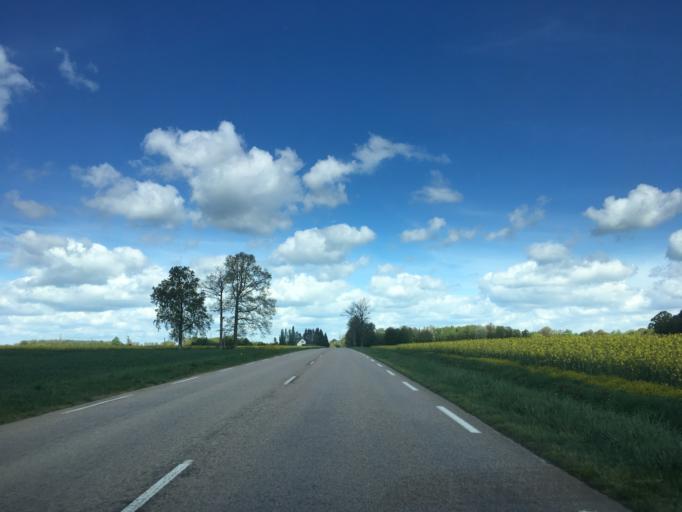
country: FR
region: Lower Normandy
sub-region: Departement de l'Orne
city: Rai
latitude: 48.7978
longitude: 0.5914
